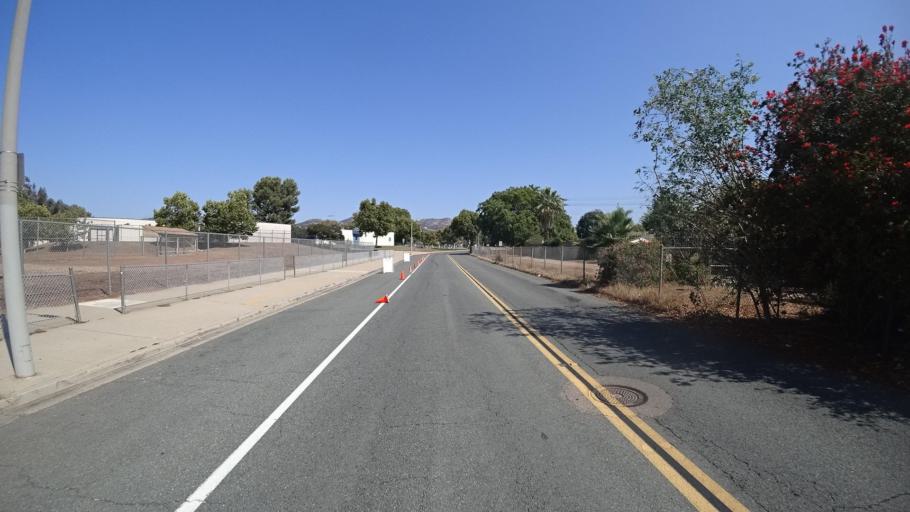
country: US
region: California
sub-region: San Diego County
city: Bostonia
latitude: 32.7965
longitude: -116.9222
